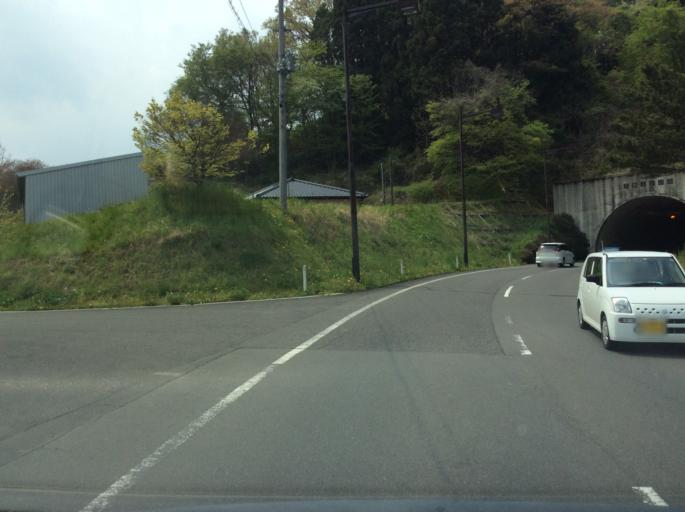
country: JP
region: Fukushima
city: Miharu
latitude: 37.3967
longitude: 140.4782
